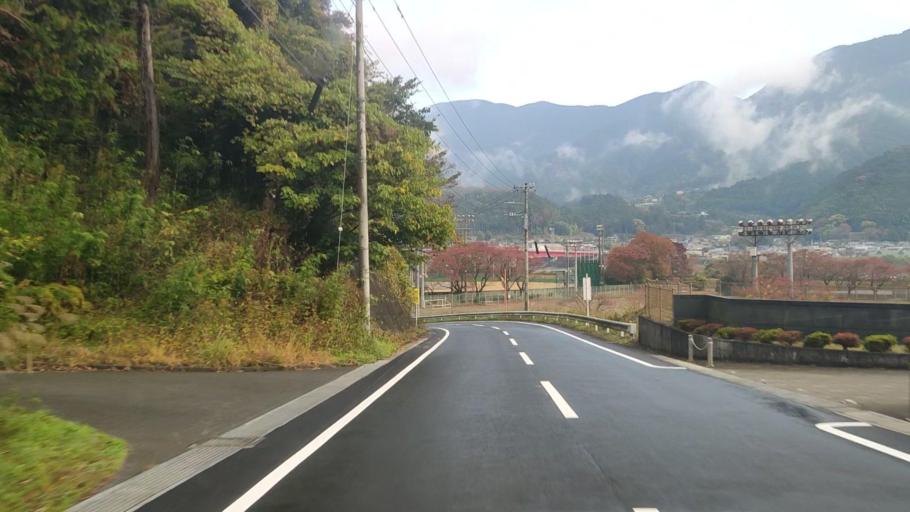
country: JP
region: Shizuoka
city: Fujinomiya
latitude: 35.2756
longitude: 138.4570
